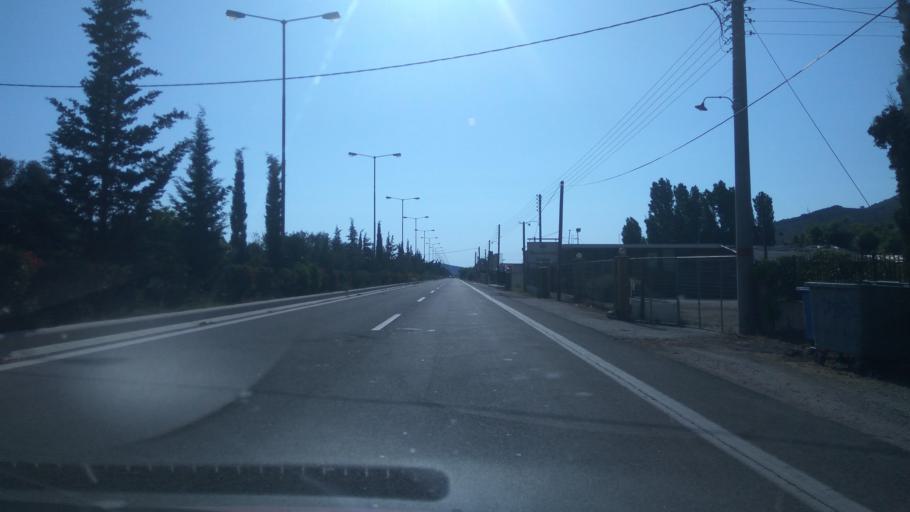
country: GR
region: Attica
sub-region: Nomarchia Anatolikis Attikis
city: Keratea
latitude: 37.8018
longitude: 24.0170
